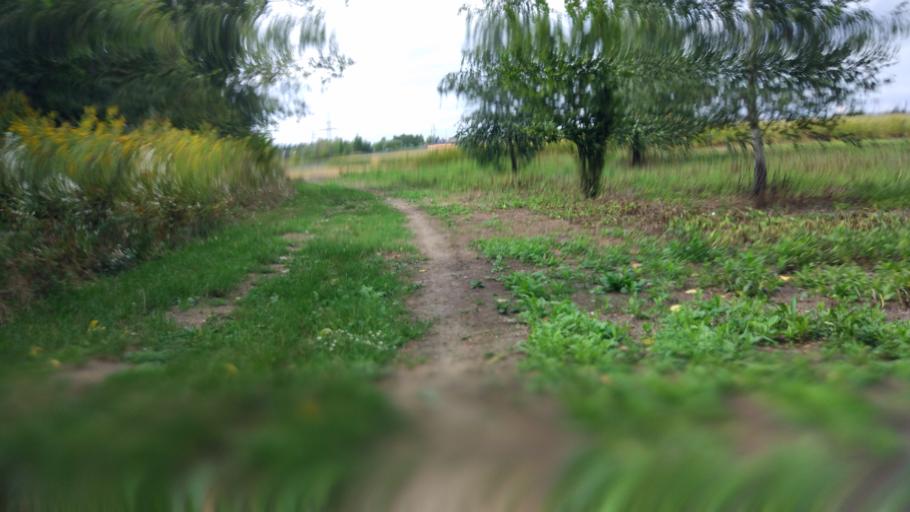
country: PL
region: Masovian Voivodeship
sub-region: Plock
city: Plock
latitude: 52.5291
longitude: 19.7435
